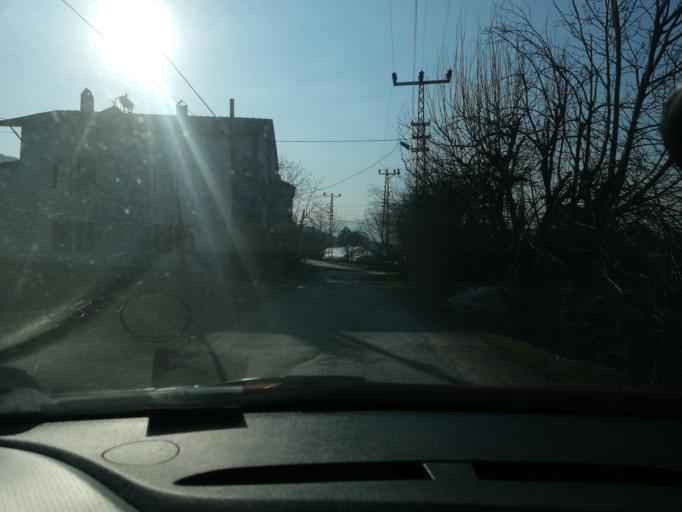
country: TR
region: Karabuk
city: Safranbolu
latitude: 41.2159
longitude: 32.7410
